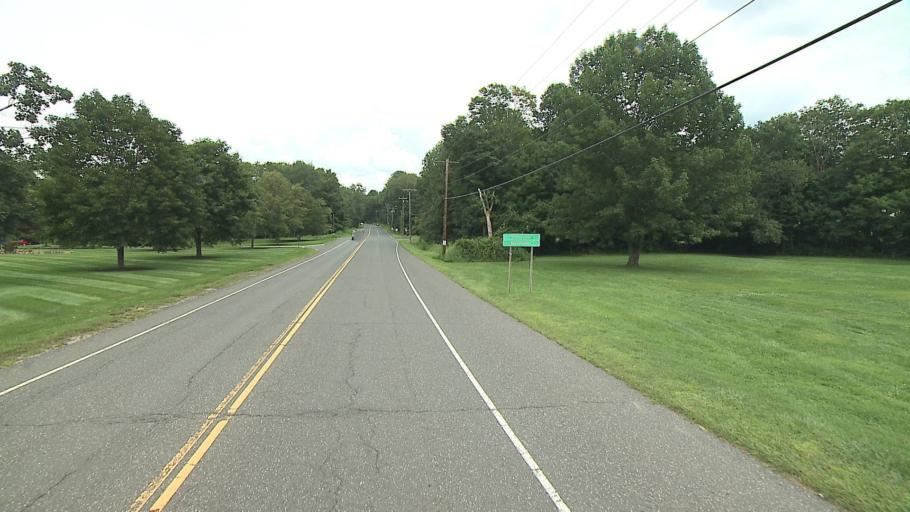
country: US
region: Connecticut
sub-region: Litchfield County
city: Woodbury Center
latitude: 41.5288
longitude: -73.2004
